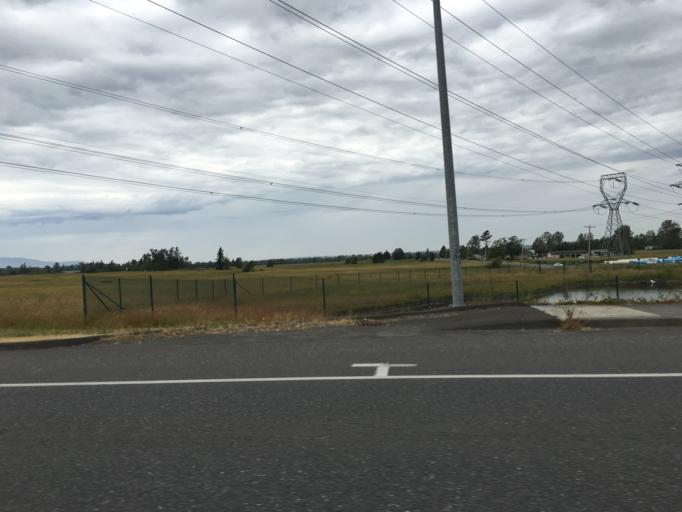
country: US
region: Washington
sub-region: Whatcom County
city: Bellingham
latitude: 48.8329
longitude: -122.4860
